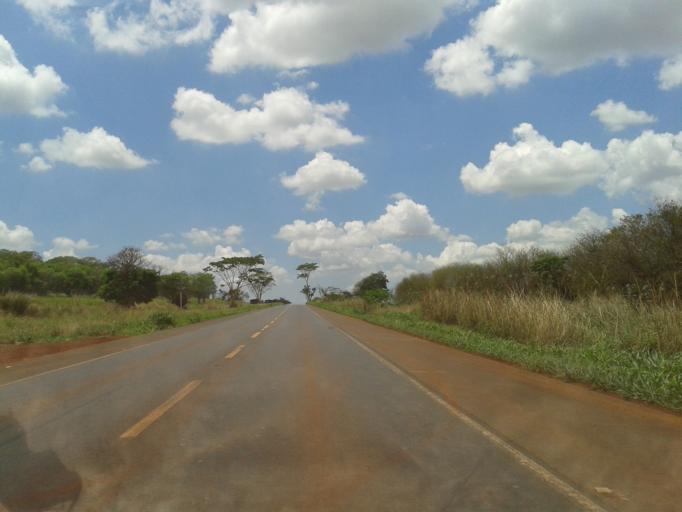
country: BR
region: Goias
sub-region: Itumbiara
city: Itumbiara
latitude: -18.3504
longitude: -49.3892
